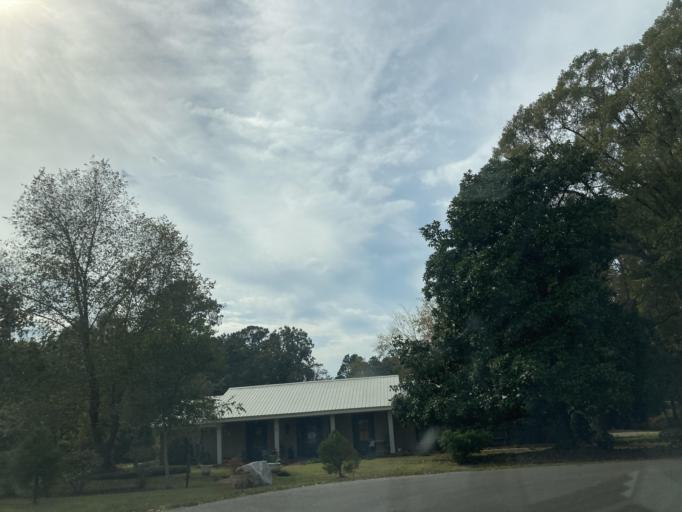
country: US
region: Mississippi
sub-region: Lamar County
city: West Hattiesburg
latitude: 31.3240
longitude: -89.4303
